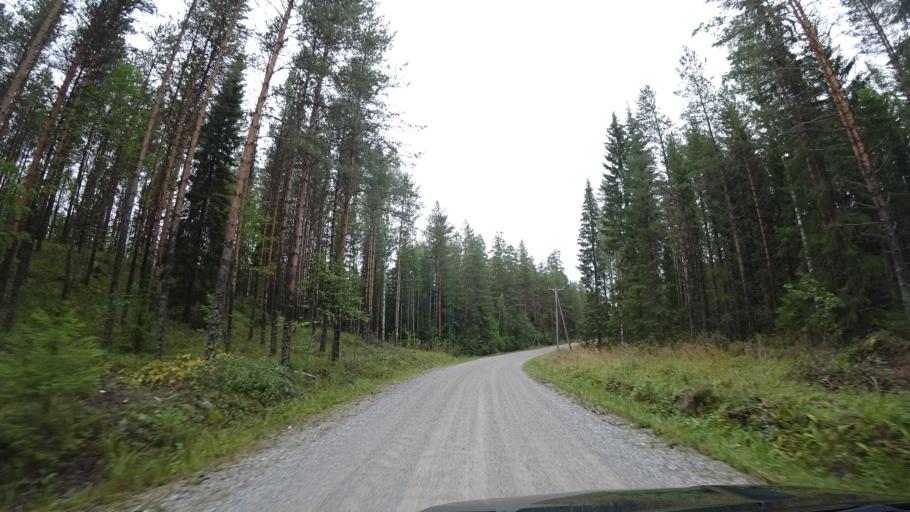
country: FI
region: Paijanne Tavastia
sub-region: Lahti
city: Auttoinen
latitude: 61.2184
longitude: 25.1383
